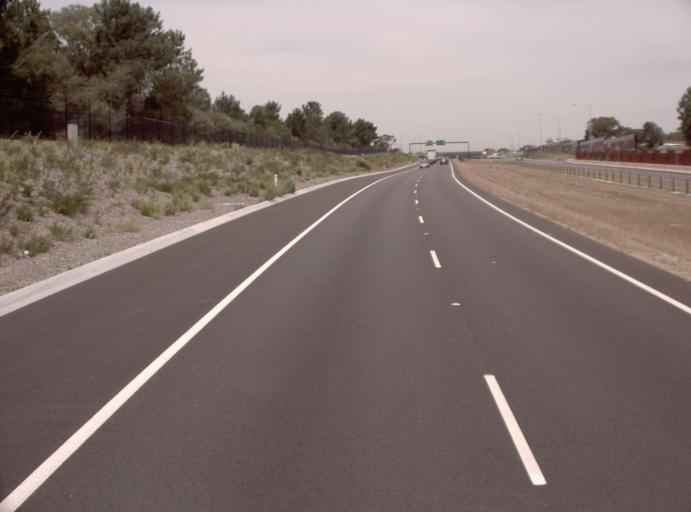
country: AU
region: Victoria
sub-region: Frankston
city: Frankston North
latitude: -38.1333
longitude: 145.1737
